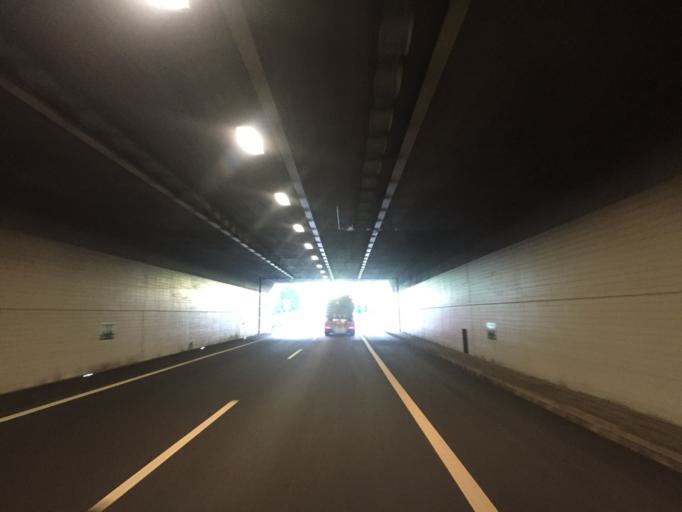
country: CH
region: Ticino
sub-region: Leventina District
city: Faido
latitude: 46.4530
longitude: 8.8280
